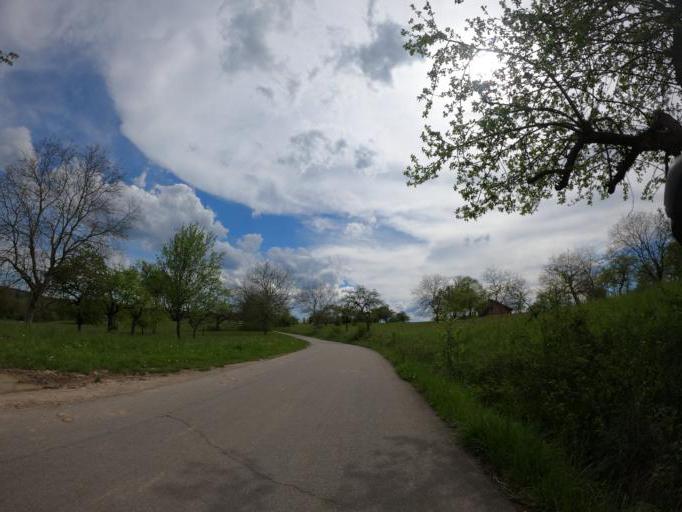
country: DE
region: Baden-Wuerttemberg
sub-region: Karlsruhe Region
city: Birkenfeld
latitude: 48.8905
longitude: 8.6016
